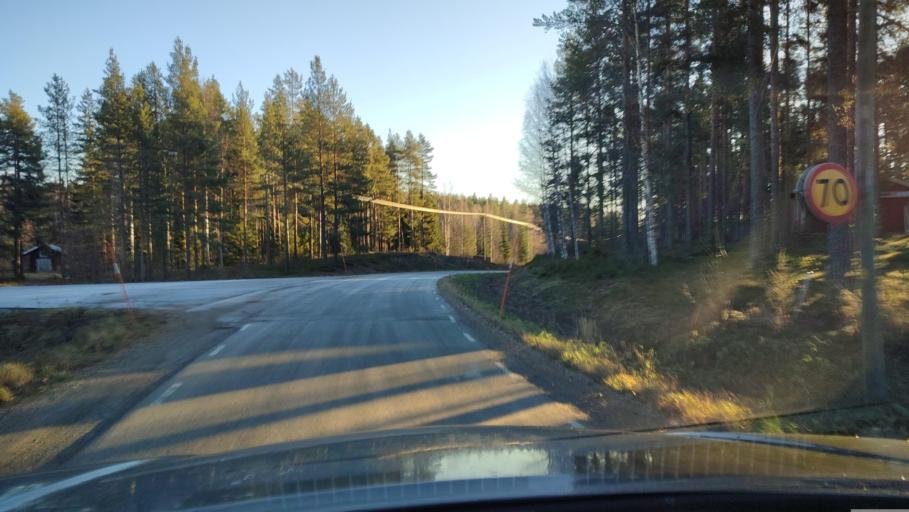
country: SE
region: Vaesterbotten
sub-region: Skelleftea Kommun
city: Viken
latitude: 64.7006
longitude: 20.9079
